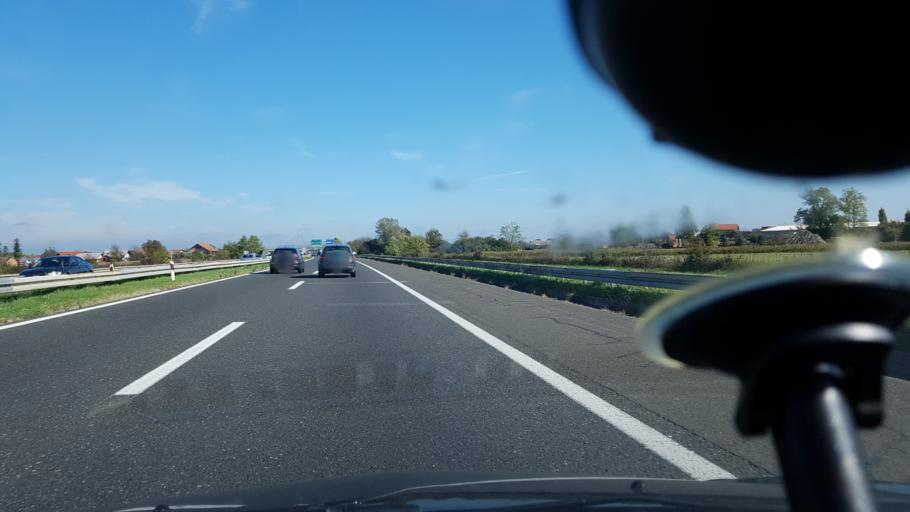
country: HR
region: Zagrebacka
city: Micevec
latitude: 45.7570
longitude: 16.0815
